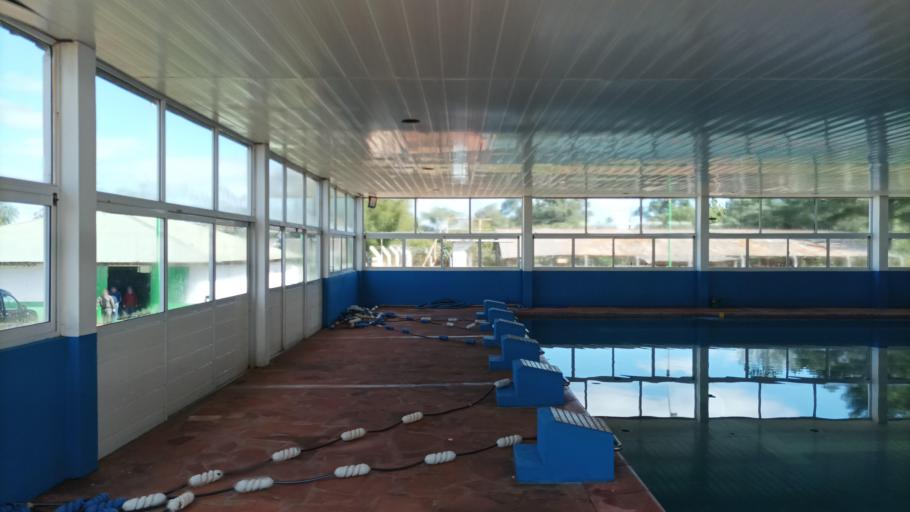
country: AR
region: Misiones
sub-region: Departamento de Apostoles
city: Apostoles
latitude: -27.9117
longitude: -55.7603
